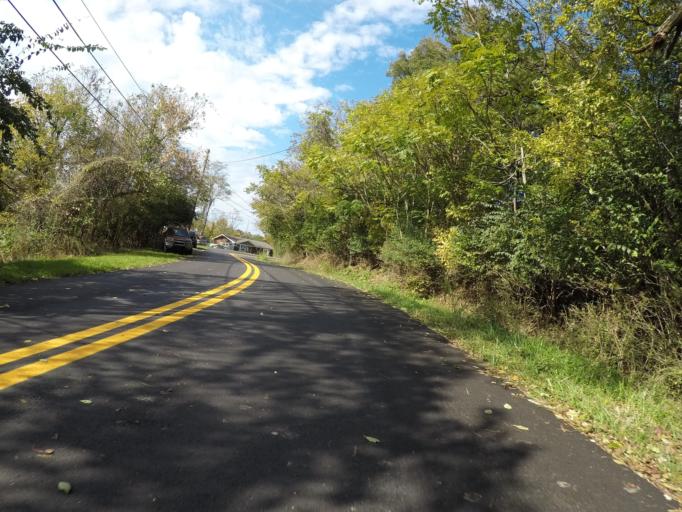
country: US
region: West Virginia
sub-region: Cabell County
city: Huntington
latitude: 38.3810
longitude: -82.4260
